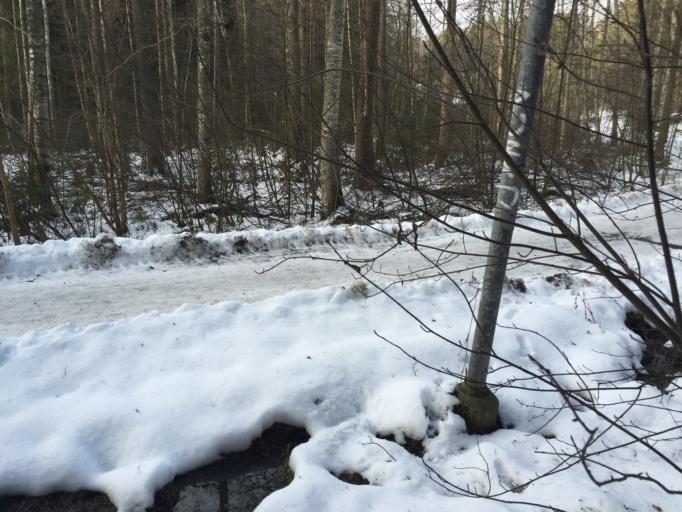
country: SE
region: Stockholm
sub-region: Salems Kommun
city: Ronninge
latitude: 59.1910
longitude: 17.7692
